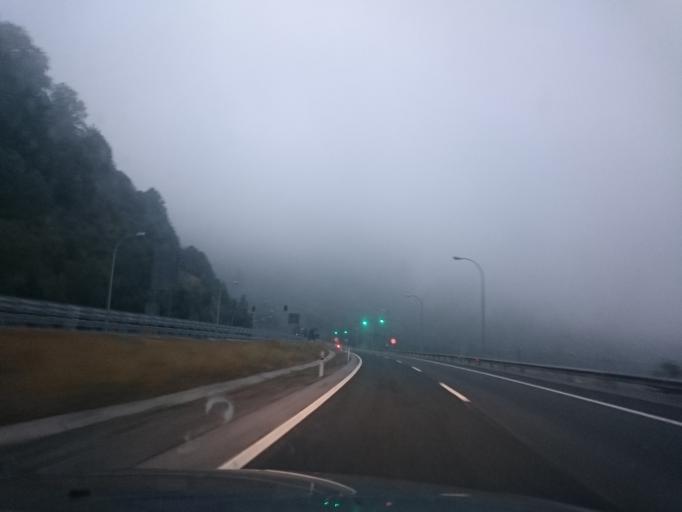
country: ES
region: Castille and Leon
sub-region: Provincia de Leon
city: Sena de Luna
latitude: 42.9916
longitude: -5.8163
